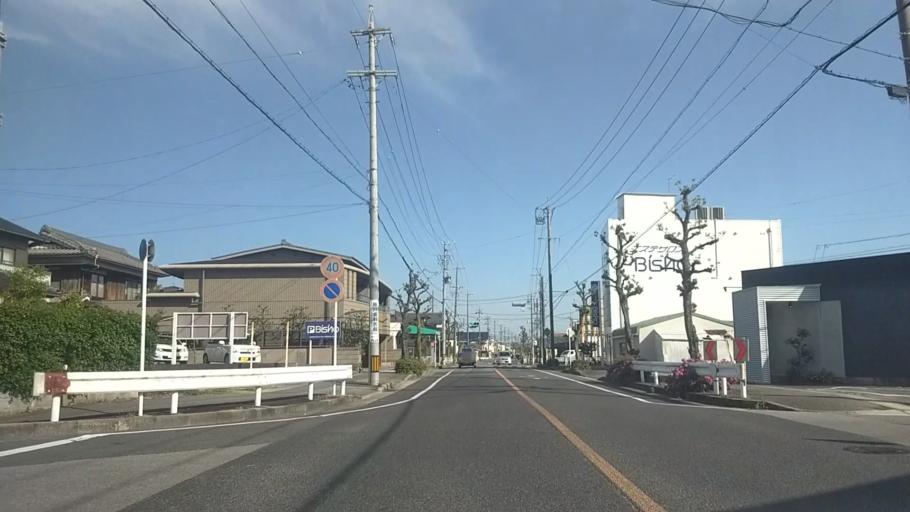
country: JP
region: Aichi
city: Anjo
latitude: 34.9517
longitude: 137.0937
